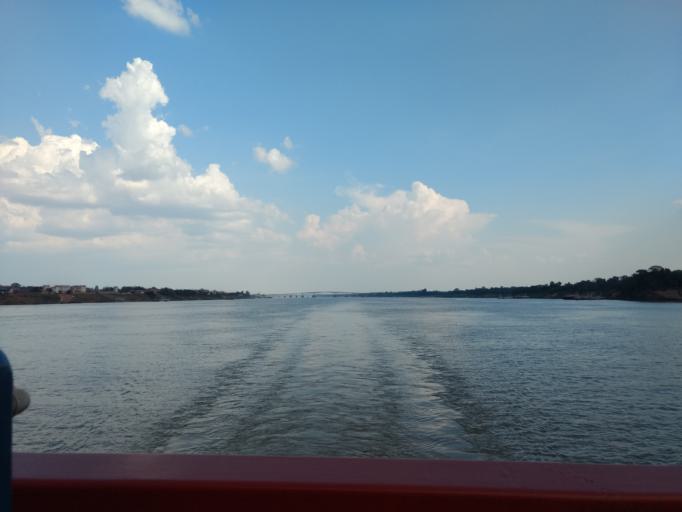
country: BR
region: Rondonia
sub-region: Porto Velho
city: Porto Velho
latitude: -8.7006
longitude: -63.9227
